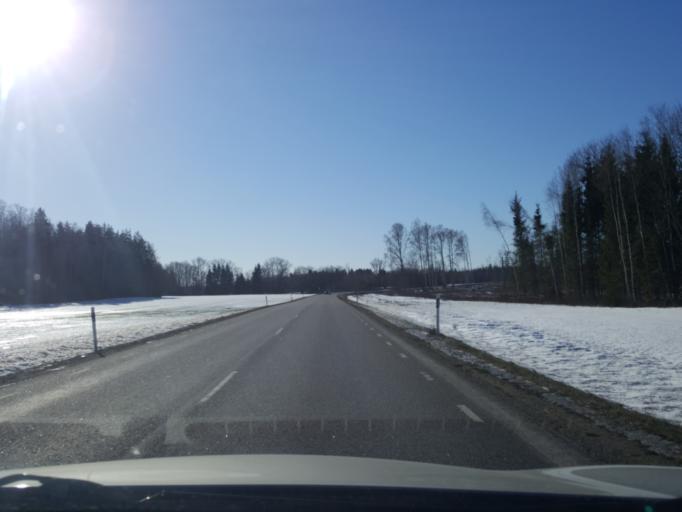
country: EE
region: Viljandimaa
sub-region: Viiratsi vald
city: Viiratsi
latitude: 58.4246
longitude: 25.6825
